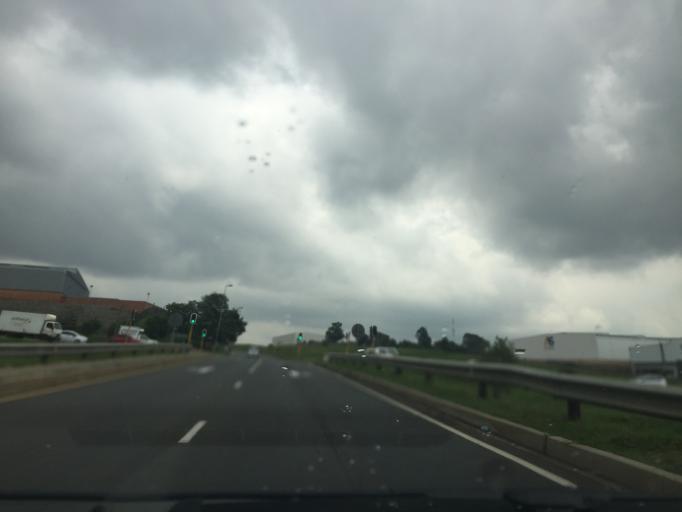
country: ZA
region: Gauteng
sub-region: City of Johannesburg Metropolitan Municipality
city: Modderfontein
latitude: -26.1052
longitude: 28.1388
